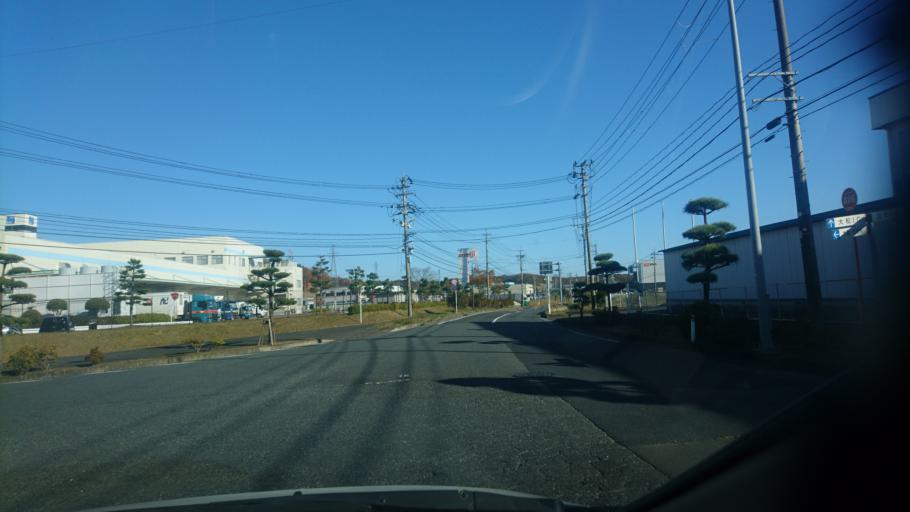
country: JP
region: Miyagi
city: Tomiya
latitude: 38.4657
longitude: 140.9213
